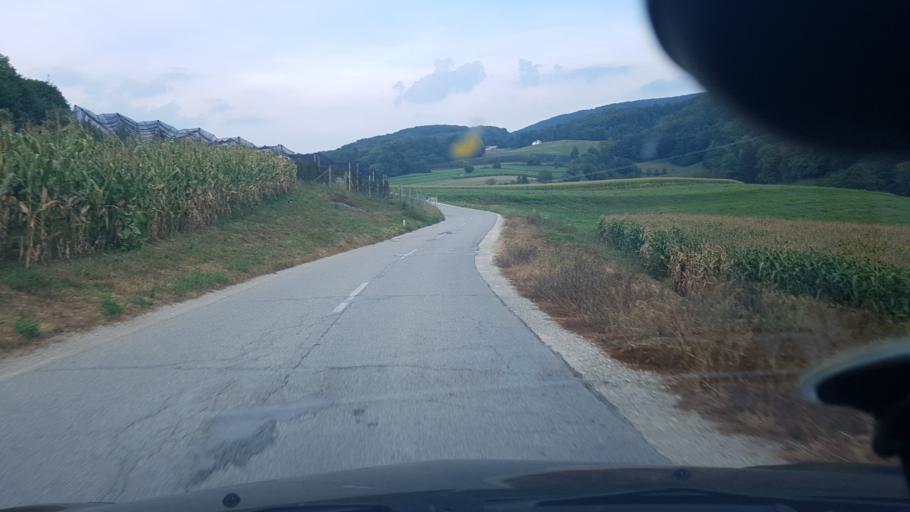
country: SI
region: Kozje
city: Kozje
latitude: 46.0296
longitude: 15.5545
